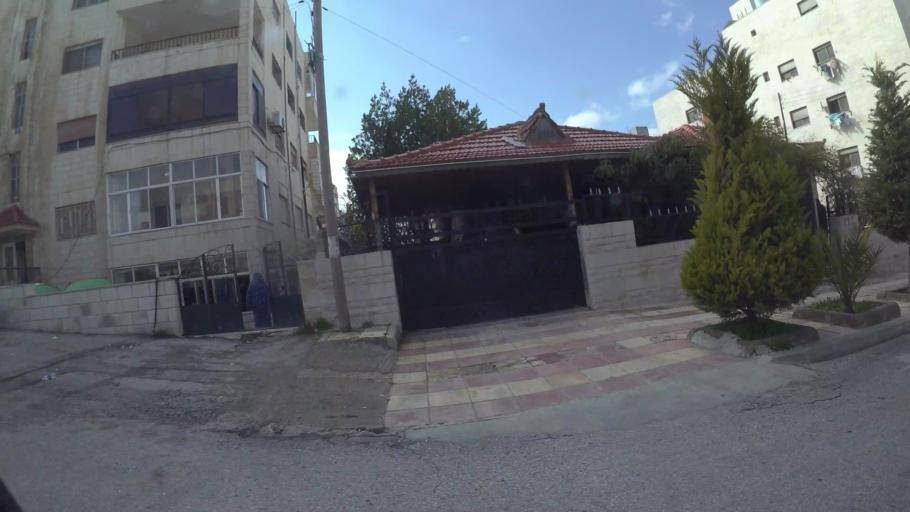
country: JO
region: Amman
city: Al Jubayhah
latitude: 32.0228
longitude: 35.8544
